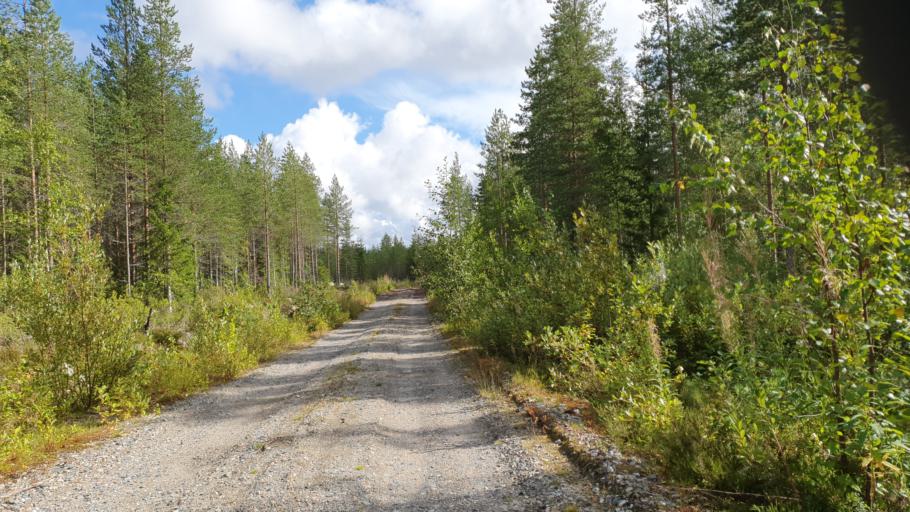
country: FI
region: Kainuu
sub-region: Kehys-Kainuu
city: Kuhmo
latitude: 64.1395
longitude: 29.3918
